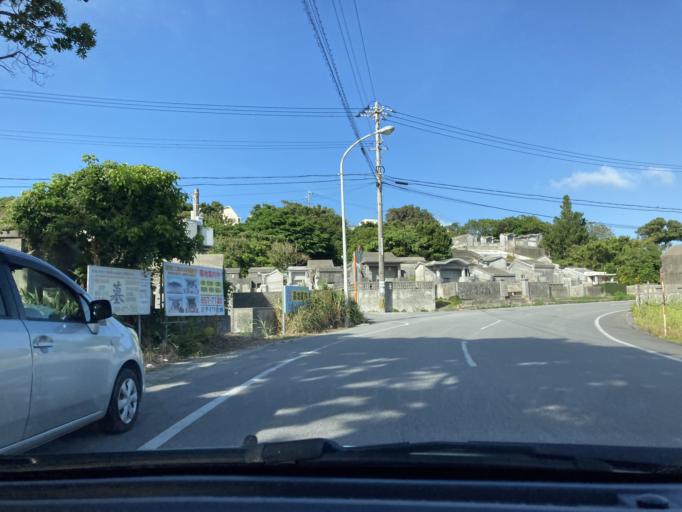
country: JP
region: Okinawa
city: Naha-shi
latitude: 26.2043
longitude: 127.7119
